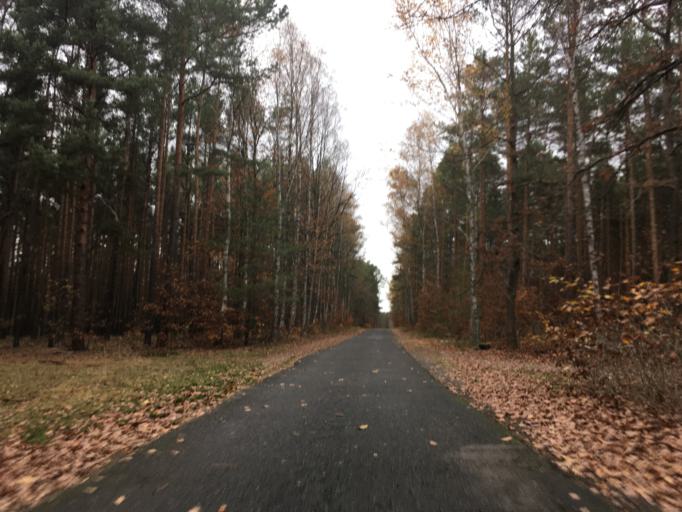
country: DE
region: Brandenburg
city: Mixdorf
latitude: 52.1783
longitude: 14.4344
